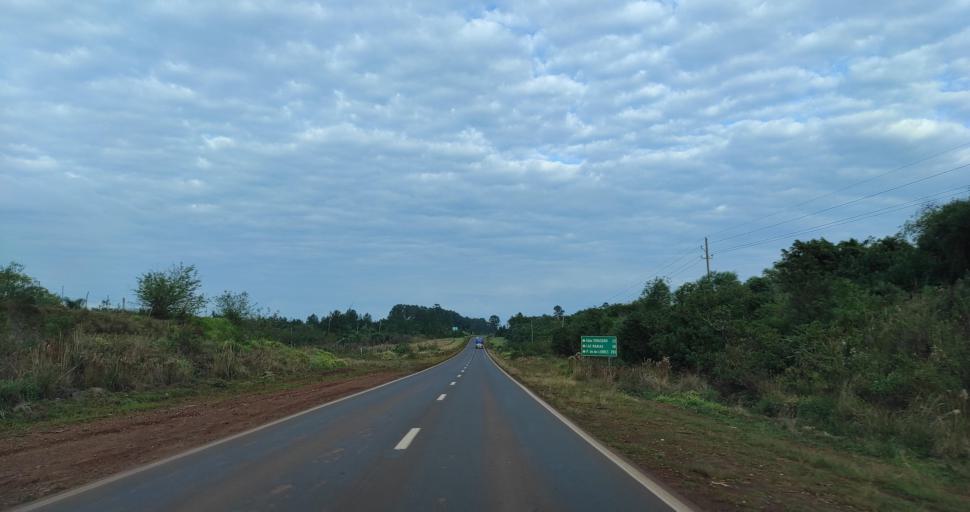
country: AR
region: Corrientes
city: Gobernador Ingeniero Valentin Virasoro
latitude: -27.9352
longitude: -55.9721
